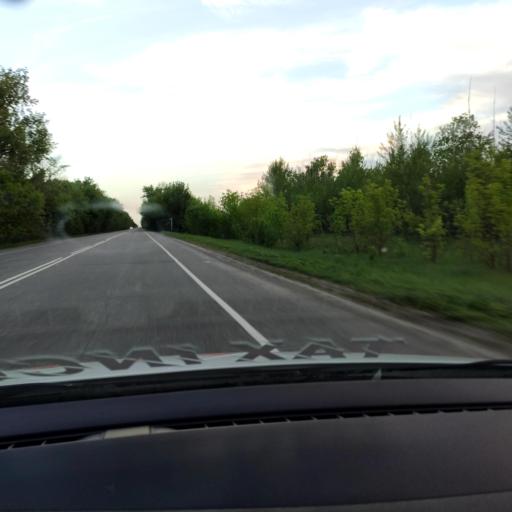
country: RU
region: Voronezj
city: Maslovka
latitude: 51.4856
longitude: 39.3075
